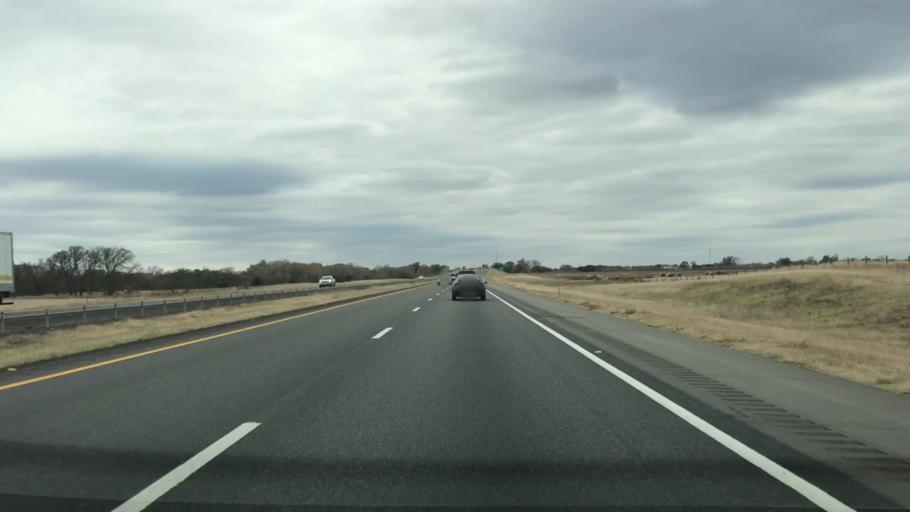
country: US
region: Oklahoma
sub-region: Beckham County
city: Elk City
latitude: 35.3857
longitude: -99.4424
